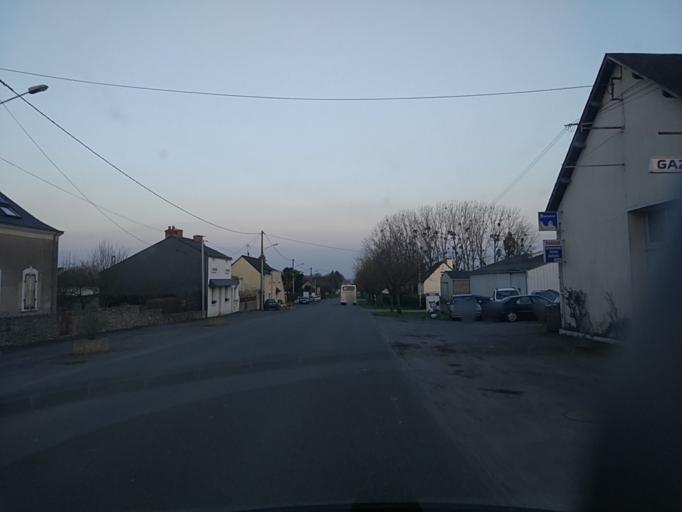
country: FR
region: Pays de la Loire
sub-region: Departement de la Mayenne
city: Meslay-du-Maine
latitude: 47.8735
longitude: -0.5175
